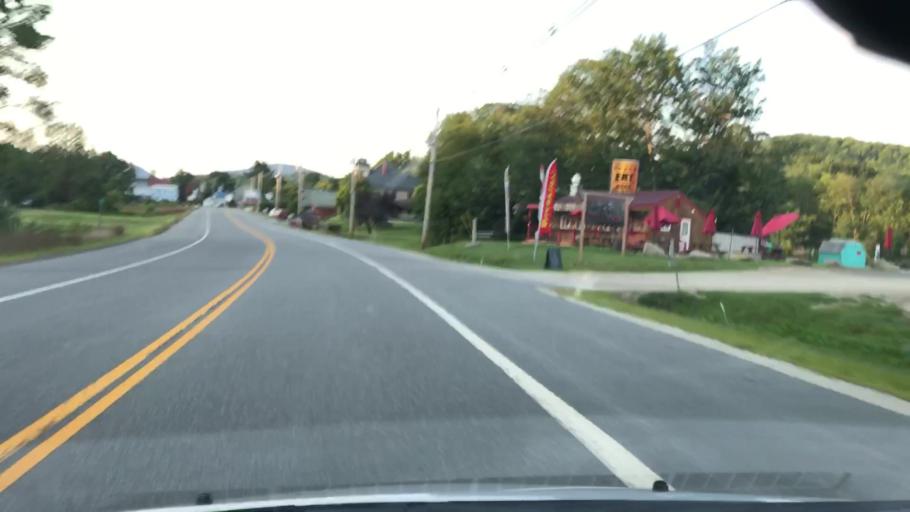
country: US
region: New Hampshire
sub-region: Grafton County
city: Rumney
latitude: 43.9121
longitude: -71.8882
